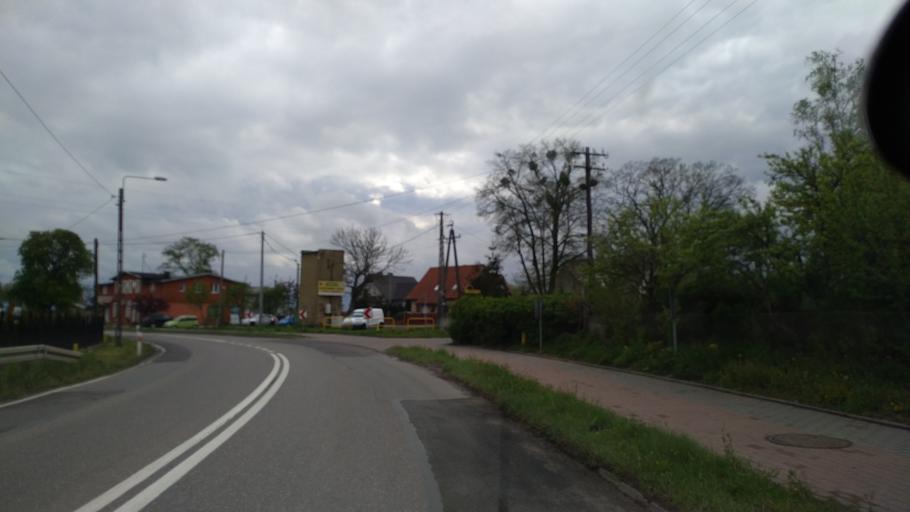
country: PL
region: Pomeranian Voivodeship
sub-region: Powiat kwidzynski
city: Kwidzyn
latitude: 53.7814
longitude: 18.9583
